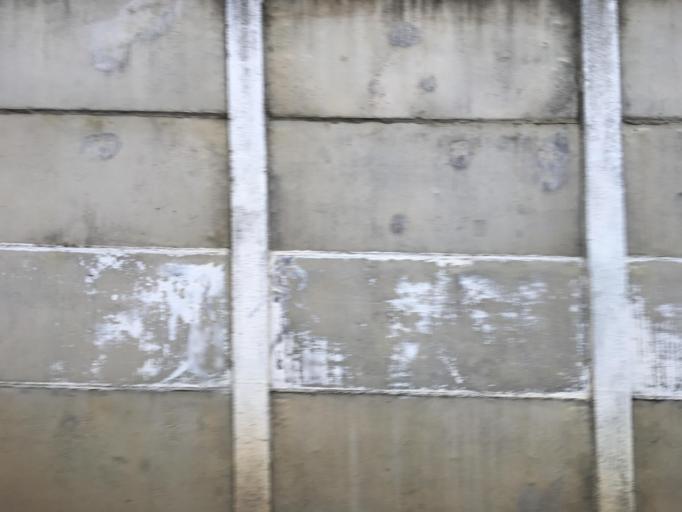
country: GT
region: Sacatepequez
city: Jocotenango
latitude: 14.5821
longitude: -90.7474
